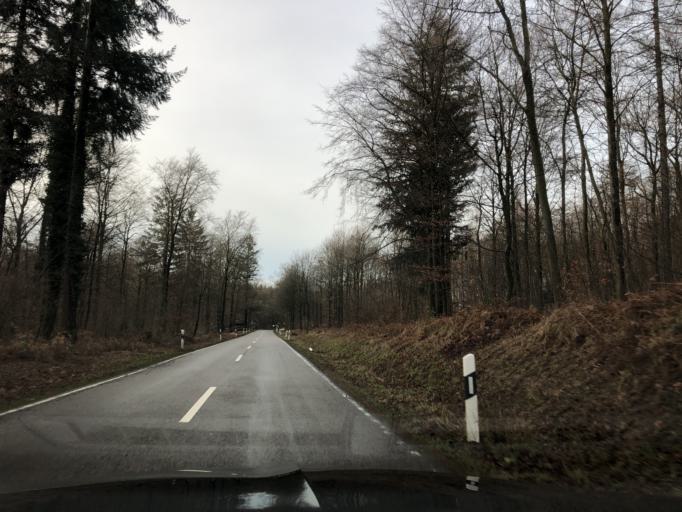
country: DE
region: Baden-Wuerttemberg
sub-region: Karlsruhe Region
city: Gaiberg
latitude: 49.3813
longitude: 8.7268
